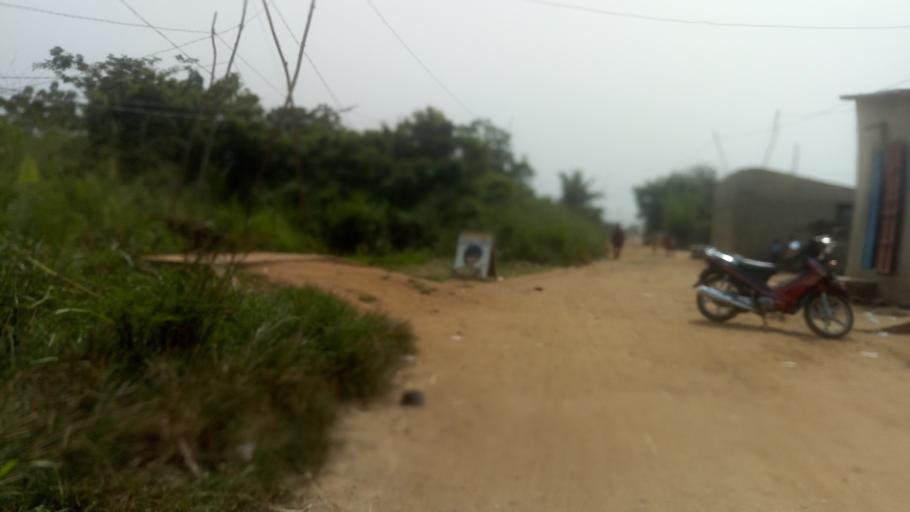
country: TG
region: Maritime
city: Lome
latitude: 6.2801
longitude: 1.2032
